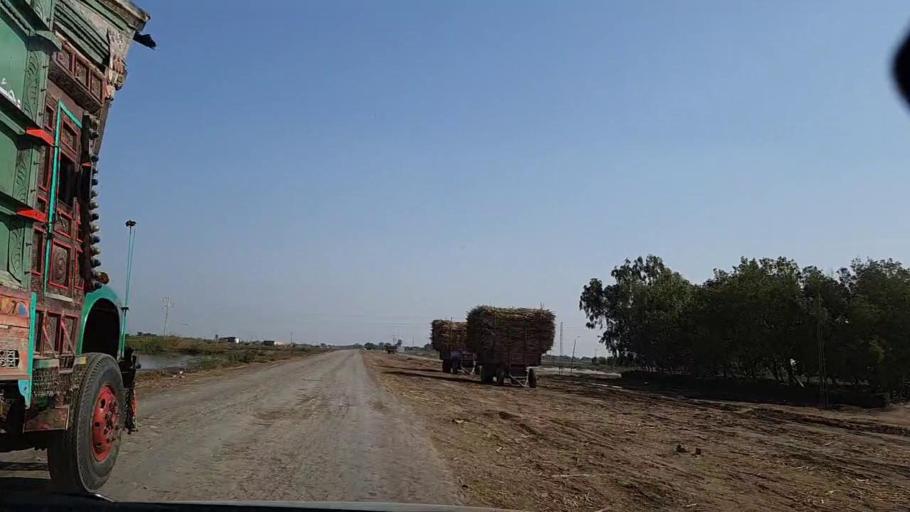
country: PK
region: Sindh
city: Digri
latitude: 25.1604
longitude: 69.0416
